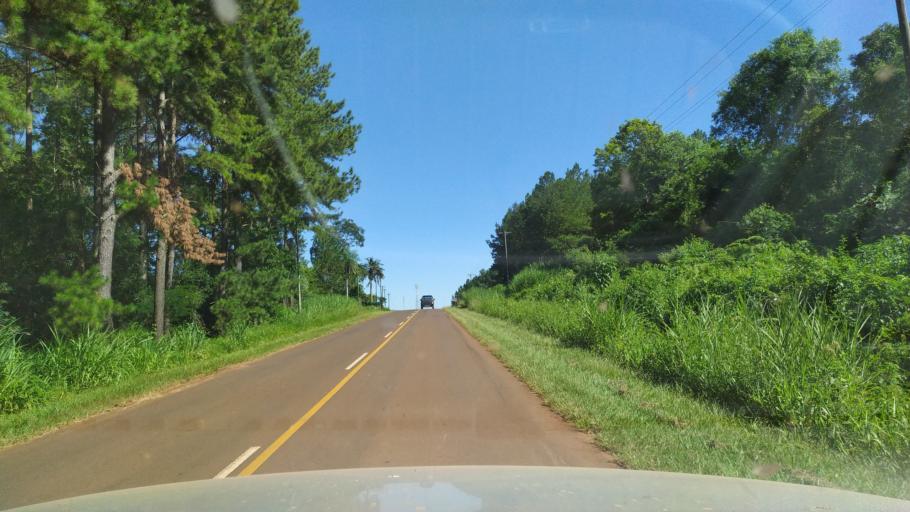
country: AR
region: Misiones
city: Caraguatay
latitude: -26.6631
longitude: -54.7331
